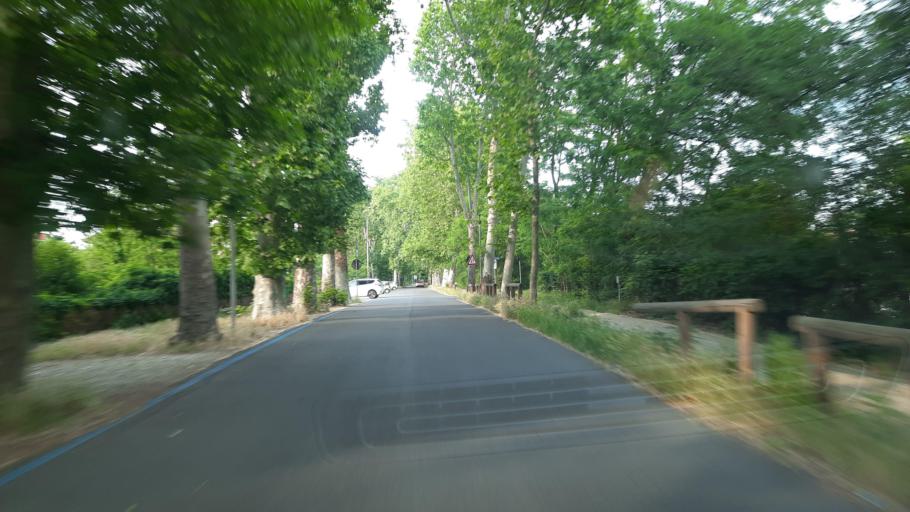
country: IT
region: Lombardy
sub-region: Provincia di Pavia
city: Pavia
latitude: 45.1917
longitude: 9.1515
